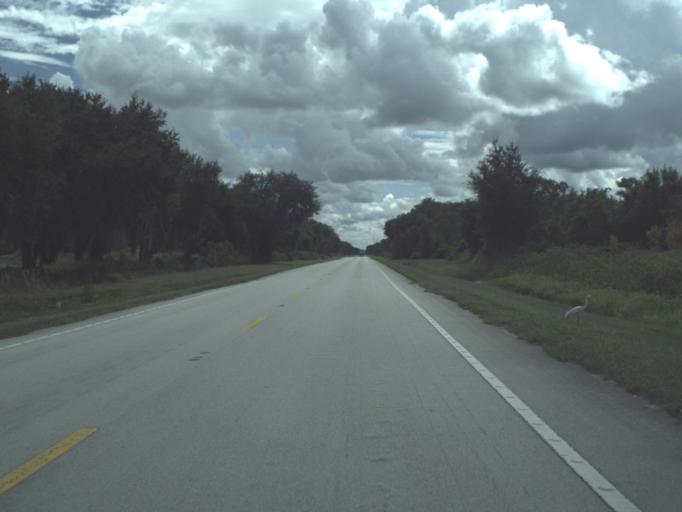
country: US
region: Florida
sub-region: DeSoto County
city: Arcadia
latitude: 27.2862
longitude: -82.0421
